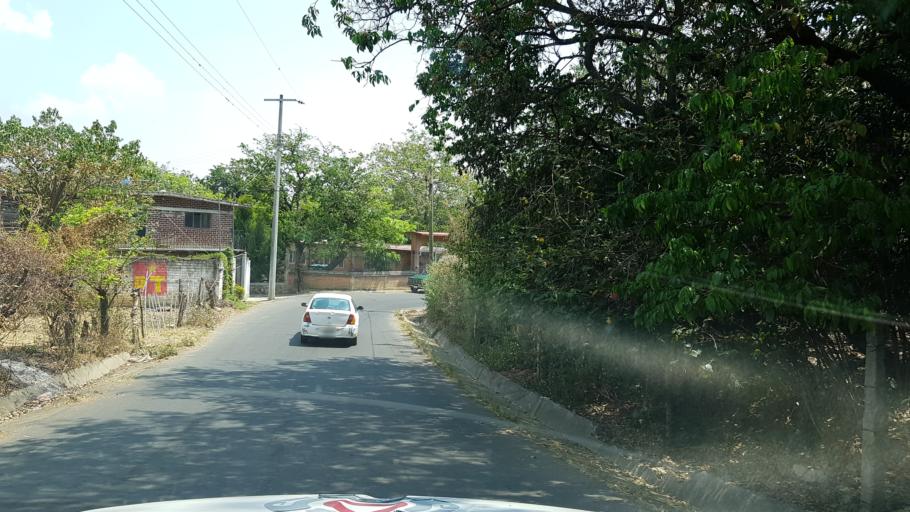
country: MX
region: Morelos
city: Ocuituco
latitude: 18.8909
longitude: -98.8108
